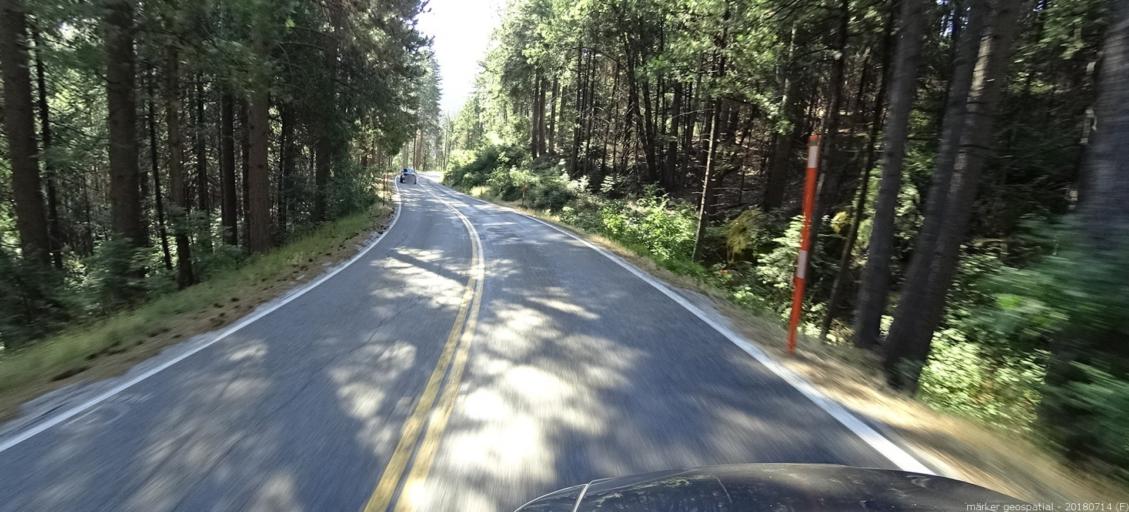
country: US
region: California
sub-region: Madera County
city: Oakhurst
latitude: 37.4273
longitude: -119.6393
